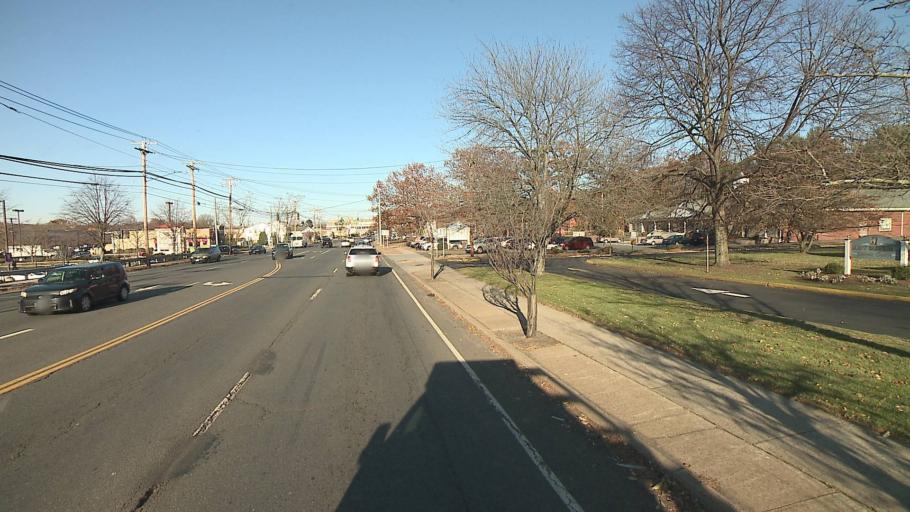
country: US
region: Connecticut
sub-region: New Haven County
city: North Haven
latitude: 41.3912
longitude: -72.8593
